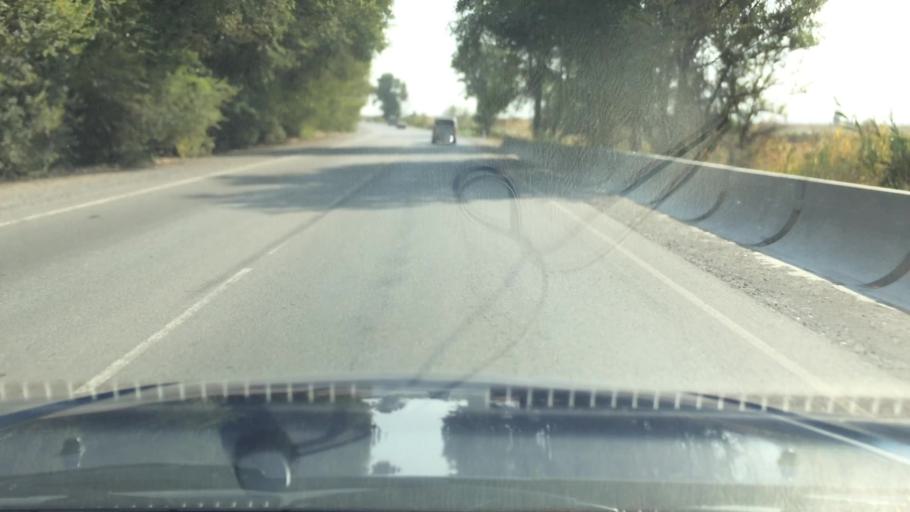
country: KG
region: Chuy
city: Lebedinovka
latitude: 42.9218
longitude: 74.7076
